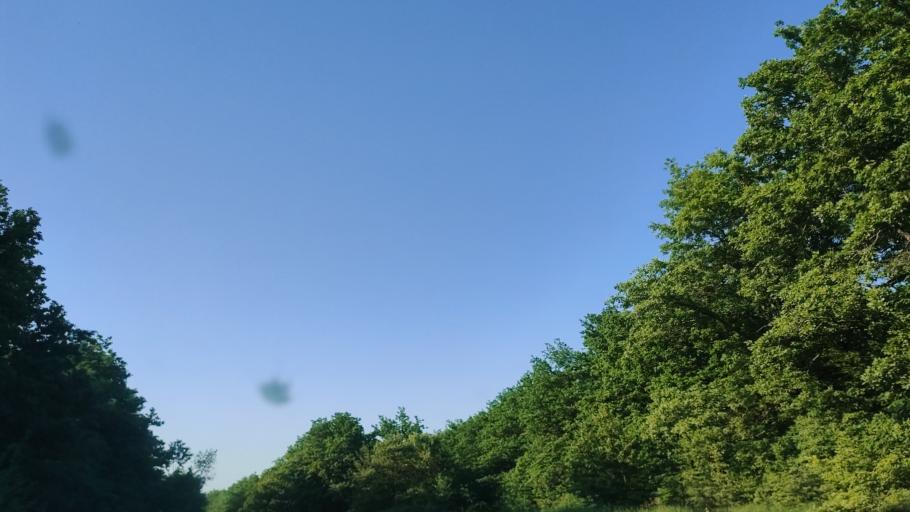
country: RU
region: Krasnodarskiy
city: Goryachiy Klyuch
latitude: 44.7075
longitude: 38.9921
